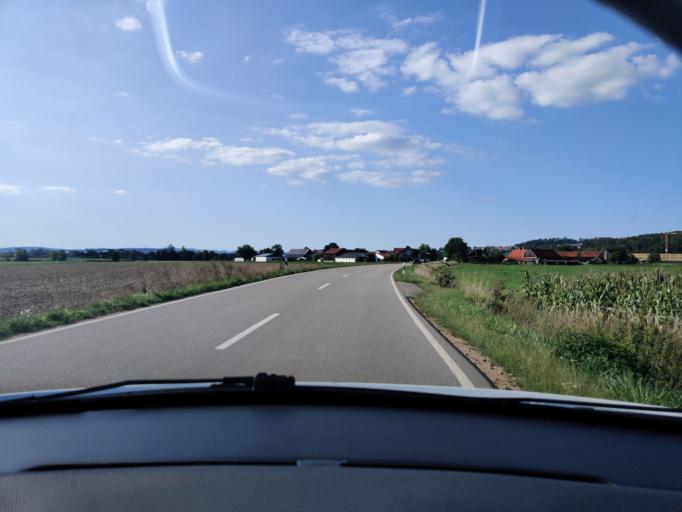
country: DE
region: Bavaria
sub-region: Upper Palatinate
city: Schwarzenfeld
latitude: 49.3727
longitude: 12.1606
